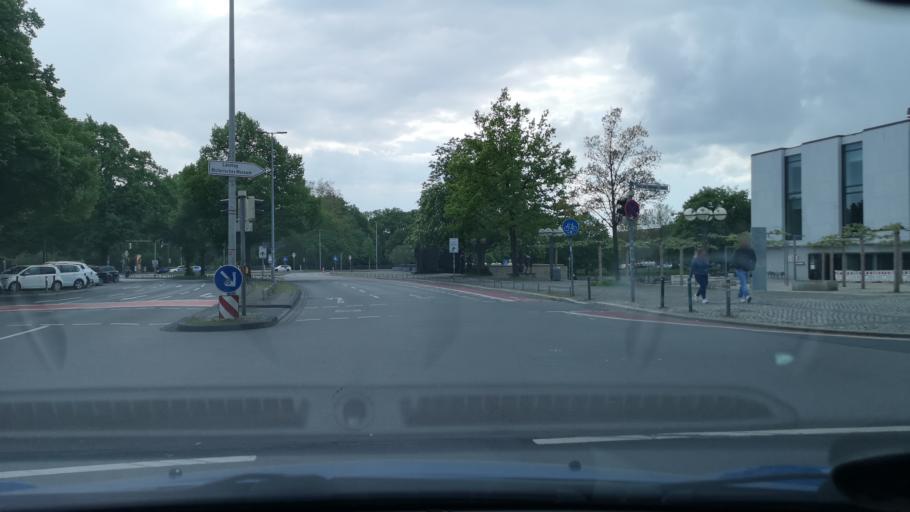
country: DE
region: Lower Saxony
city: Hannover
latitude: 52.3702
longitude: 9.7350
